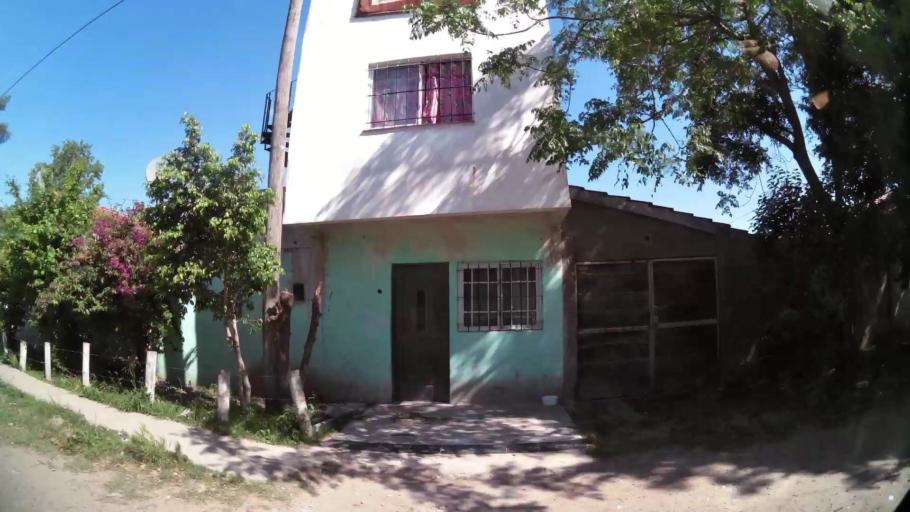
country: AR
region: Buenos Aires F.D.
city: Villa Lugano
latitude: -34.7055
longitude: -58.4751
